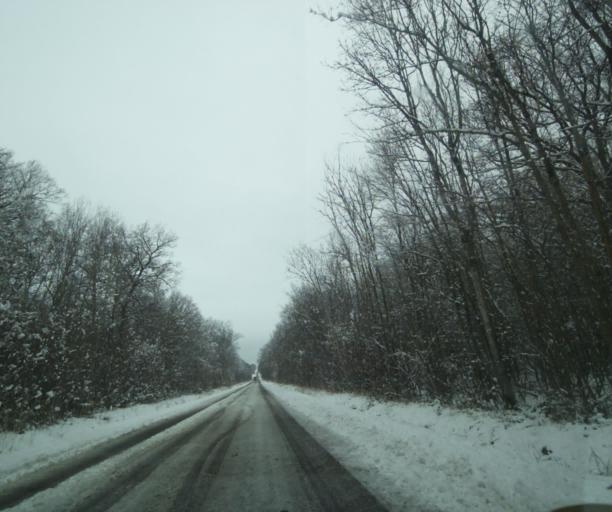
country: FR
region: Champagne-Ardenne
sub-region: Departement de la Haute-Marne
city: Montier-en-Der
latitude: 48.5176
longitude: 4.7472
